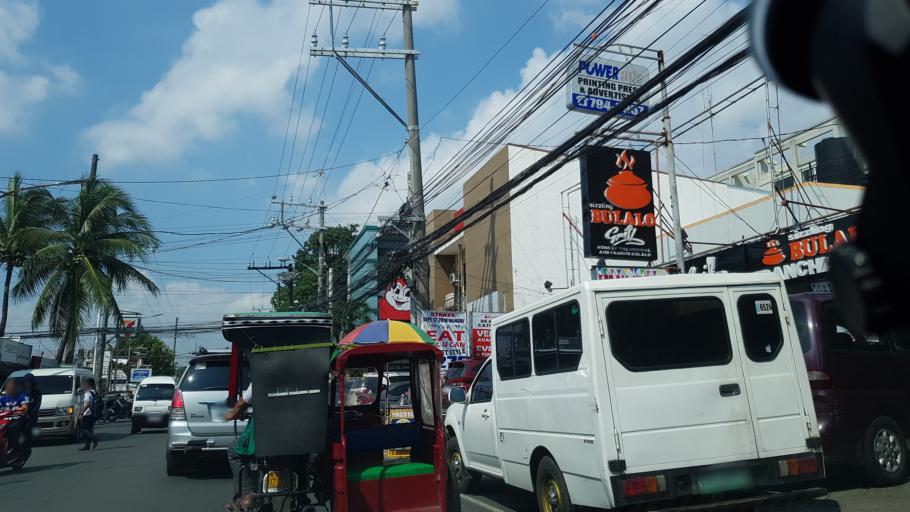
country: PH
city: Sambayanihan People's Village
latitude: 14.4699
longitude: 121.0216
